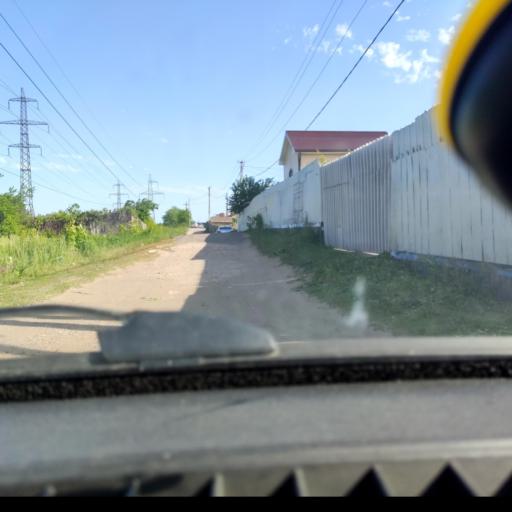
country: RU
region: Samara
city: Zhigulevsk
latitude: 53.4946
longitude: 49.4980
